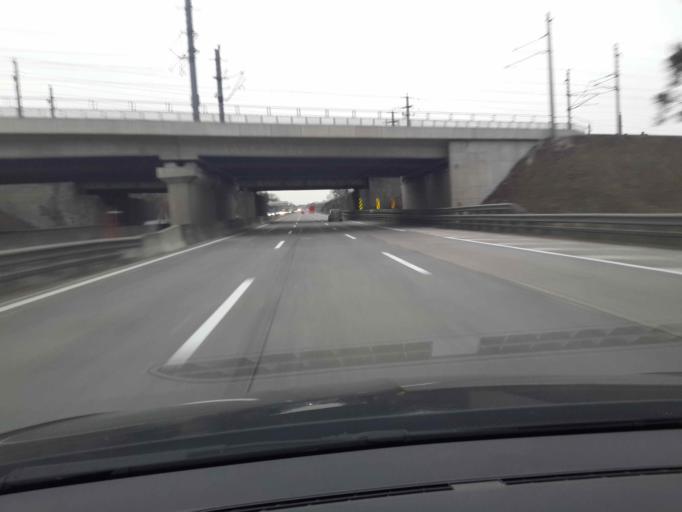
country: AT
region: Lower Austria
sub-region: Politischer Bezirk Amstetten
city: Ennsdorf
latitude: 48.1988
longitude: 14.5115
